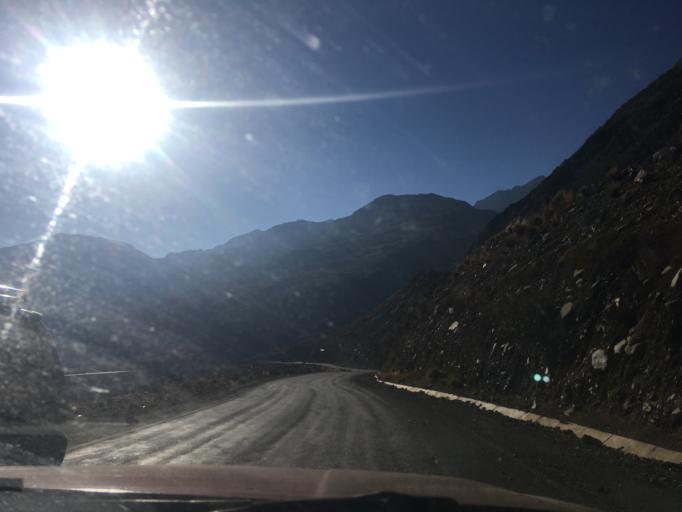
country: BO
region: La Paz
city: Quime
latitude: -17.0272
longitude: -67.2909
